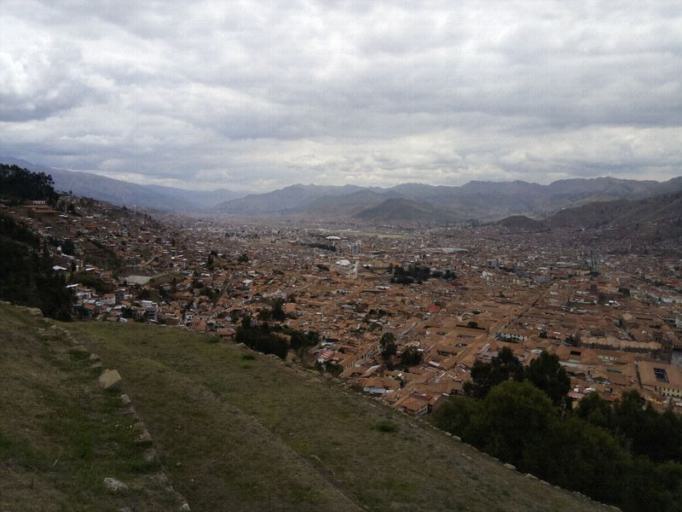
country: PE
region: Cusco
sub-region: Provincia de Cusco
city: Cusco
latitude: -13.5110
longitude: -71.9805
